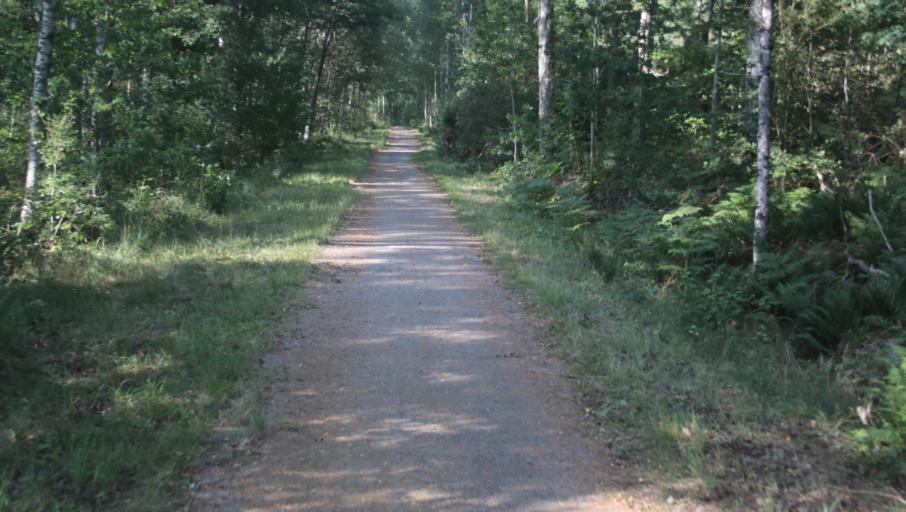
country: SE
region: Blekinge
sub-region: Karlshamns Kommun
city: Svangsta
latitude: 56.3217
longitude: 14.7054
